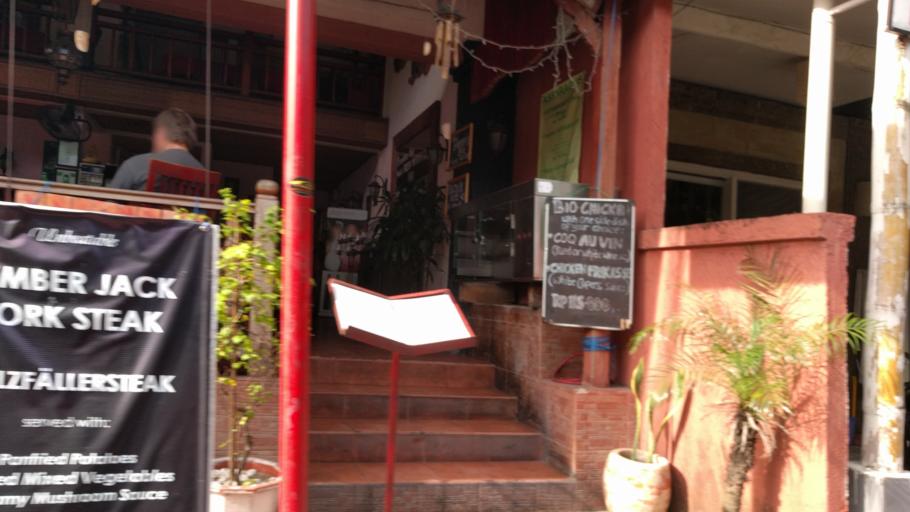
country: ID
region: Bali
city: Kuta
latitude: -8.6972
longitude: 115.1701
